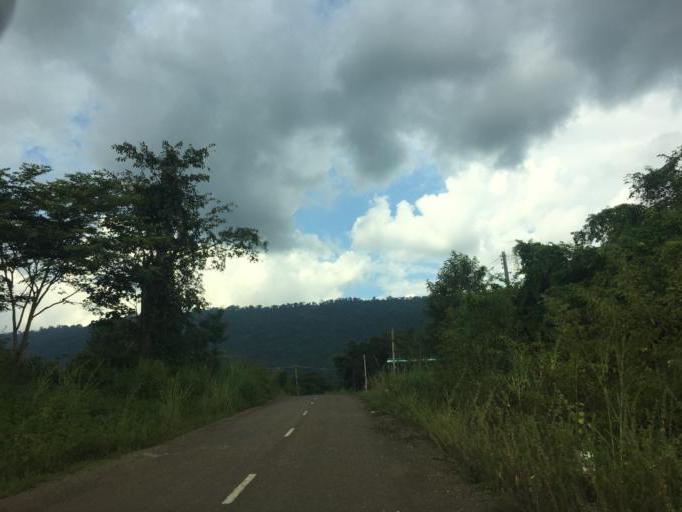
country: TH
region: Nong Khai
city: Sangkhom
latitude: 18.1476
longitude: 102.2720
